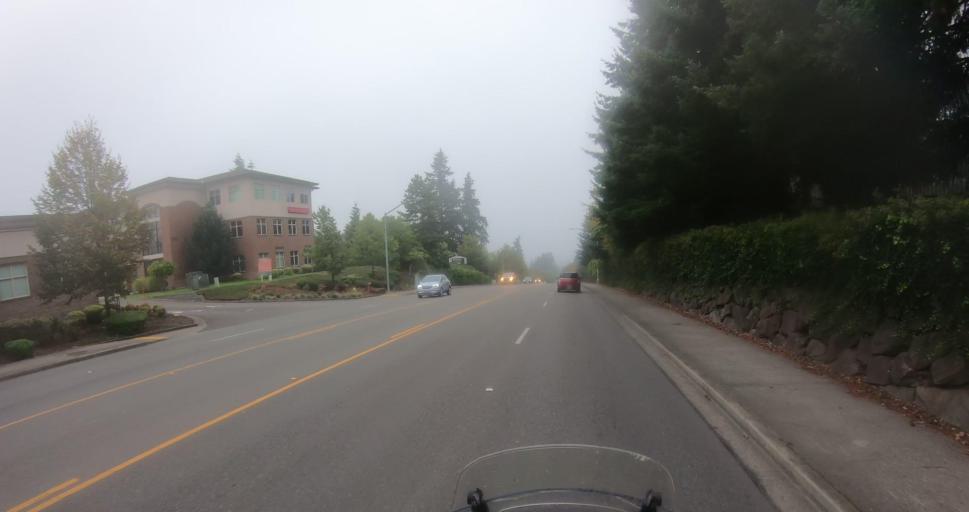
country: US
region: Washington
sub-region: Pierce County
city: Puyallup
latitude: 47.1635
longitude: -122.2932
